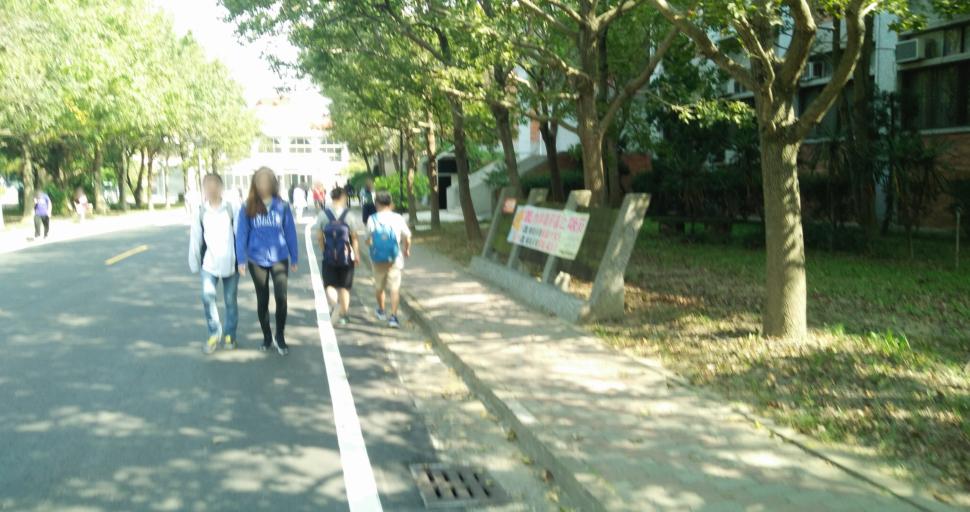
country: TW
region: Taiwan
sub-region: Hsinchu
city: Hsinchu
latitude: 24.7581
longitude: 120.9540
